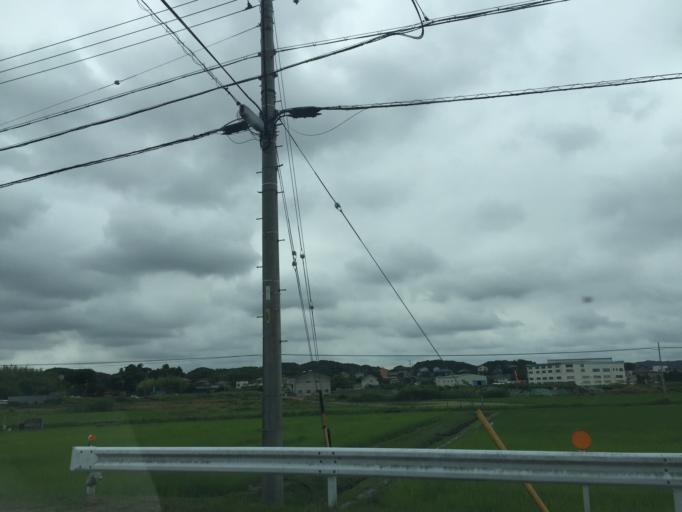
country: JP
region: Shizuoka
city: Fukuroi
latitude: 34.7683
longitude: 137.9302
